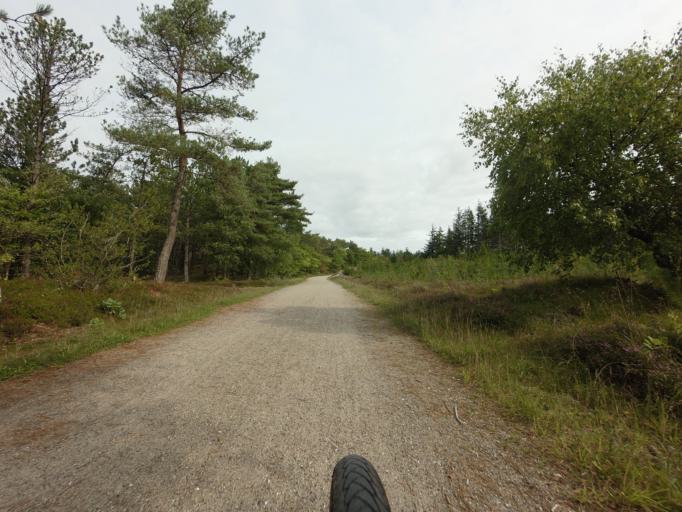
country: DK
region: North Denmark
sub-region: Hjorring Kommune
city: Sindal
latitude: 57.6050
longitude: 10.2406
